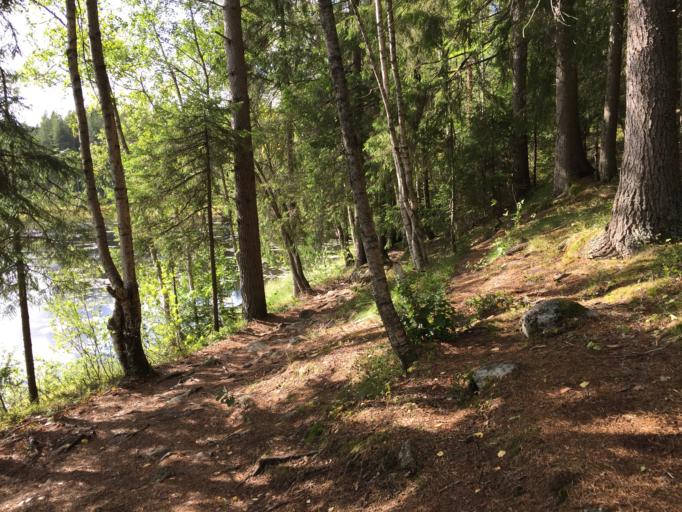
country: NO
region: Akershus
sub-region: Raelingen
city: Fjerdingby
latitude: 59.9099
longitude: 11.0301
